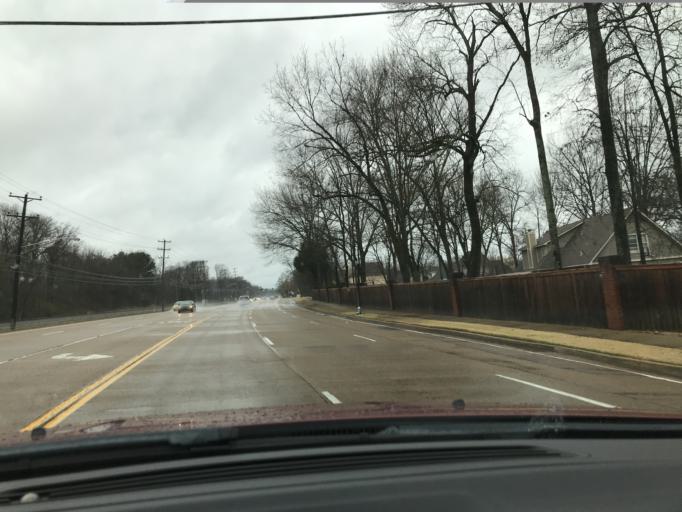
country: US
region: Tennessee
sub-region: Shelby County
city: Collierville
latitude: 35.0483
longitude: -89.7208
